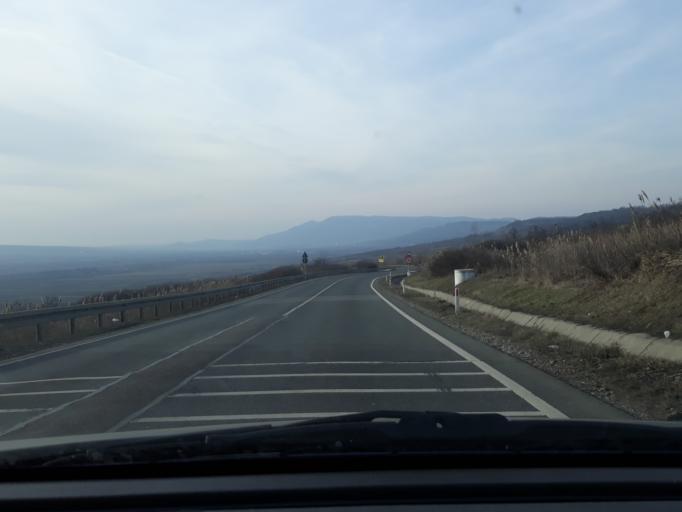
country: RO
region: Salaj
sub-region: Comuna Varsolt
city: Varsolt
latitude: 47.2151
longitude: 22.9303
